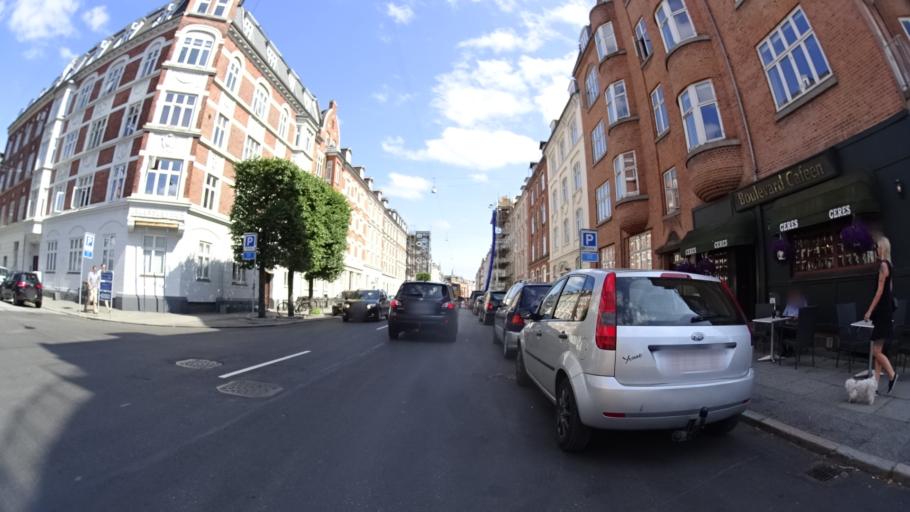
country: DK
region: Central Jutland
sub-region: Arhus Kommune
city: Arhus
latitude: 56.1450
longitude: 10.1994
